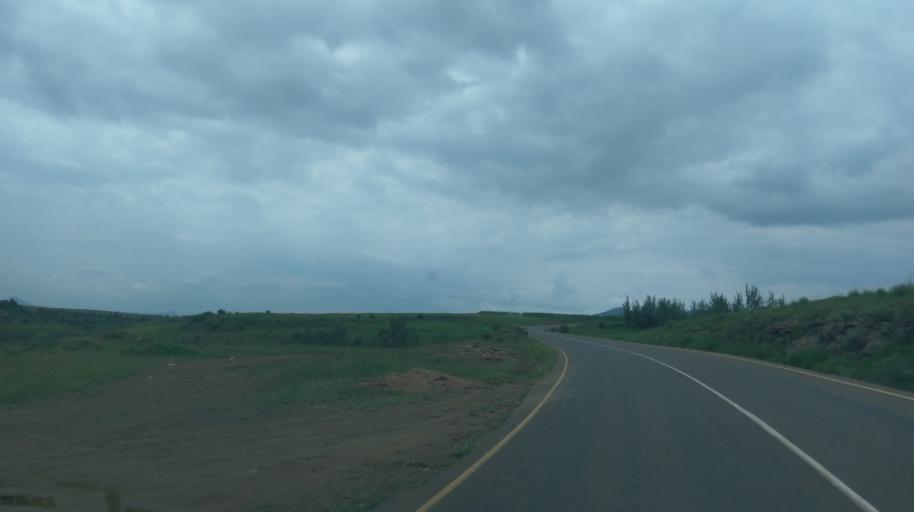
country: LS
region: Leribe
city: Leribe
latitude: -29.0360
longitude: 28.2525
